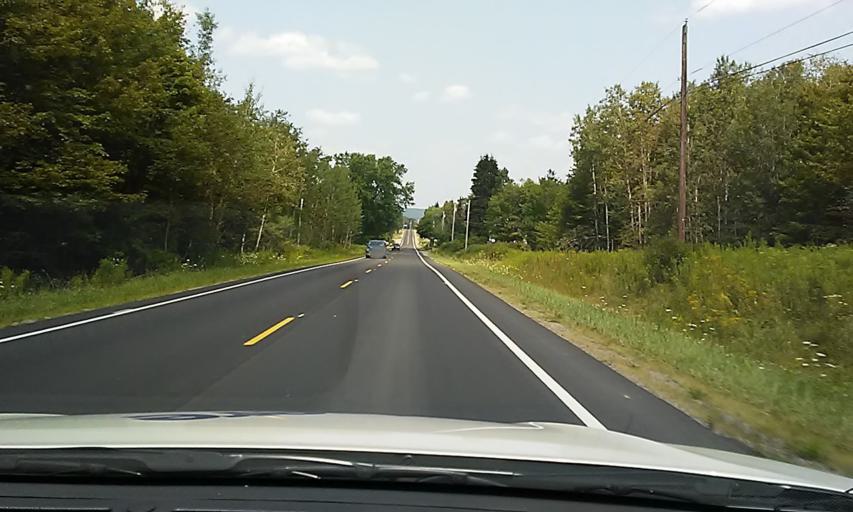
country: US
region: Pennsylvania
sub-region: Elk County
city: Saint Marys
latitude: 41.4365
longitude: -78.5082
